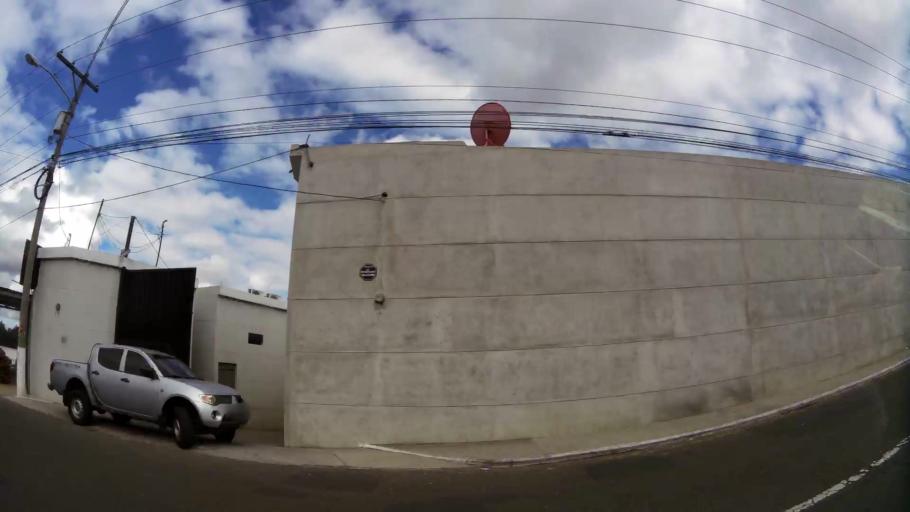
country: GT
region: Guatemala
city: Mixco
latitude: 14.6284
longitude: -90.6019
